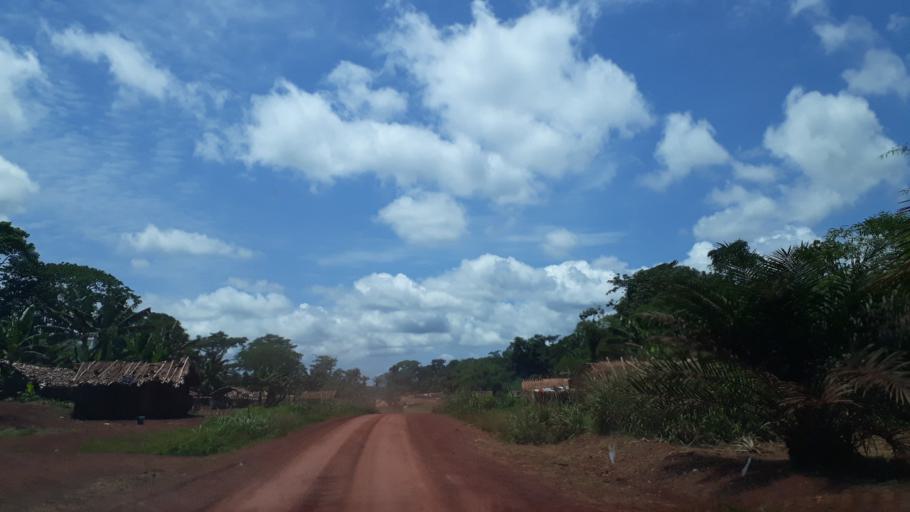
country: CD
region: Eastern Province
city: Kisangani
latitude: 0.5481
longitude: 25.9240
